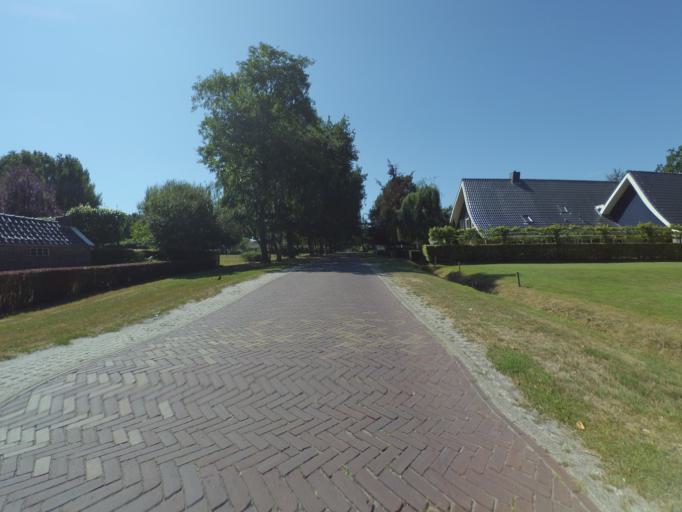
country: NL
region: Drenthe
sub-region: Gemeente Aa en Hunze
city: Anloo
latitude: 52.9350
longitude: 6.6694
